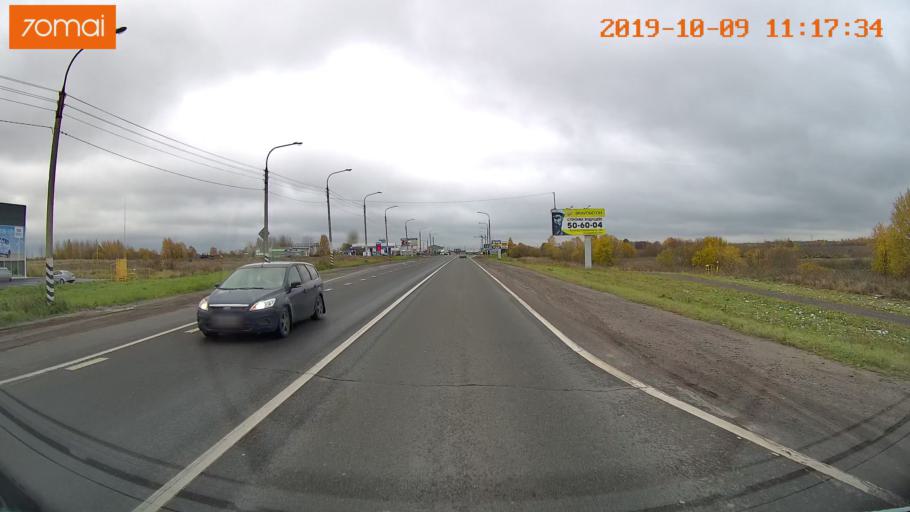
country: RU
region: Vologda
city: Vologda
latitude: 59.1736
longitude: 39.9013
